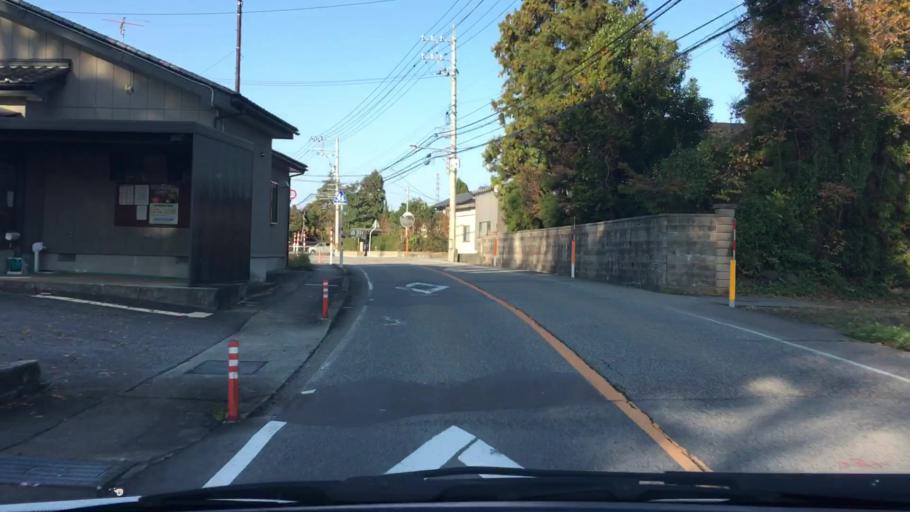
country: JP
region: Toyama
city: Kamiichi
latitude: 36.7070
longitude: 137.3070
